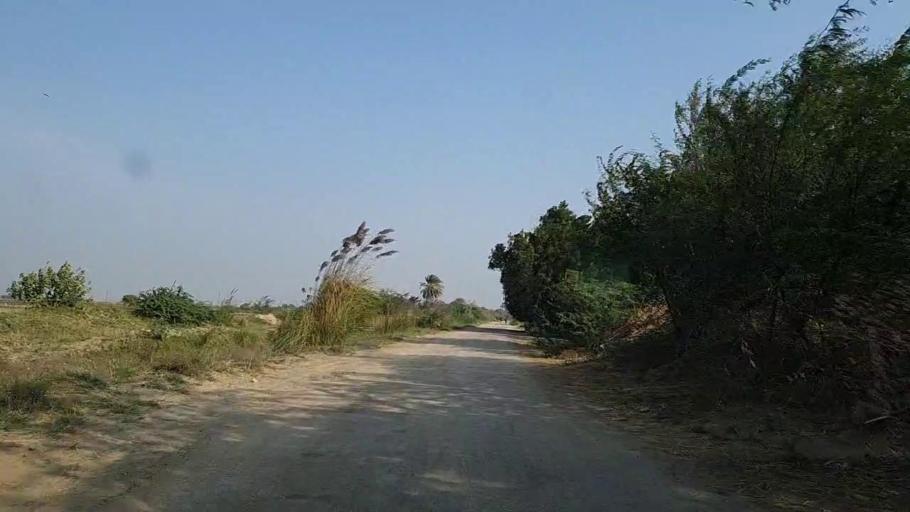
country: PK
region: Sindh
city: Mirpur Sakro
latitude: 24.5952
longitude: 67.6015
